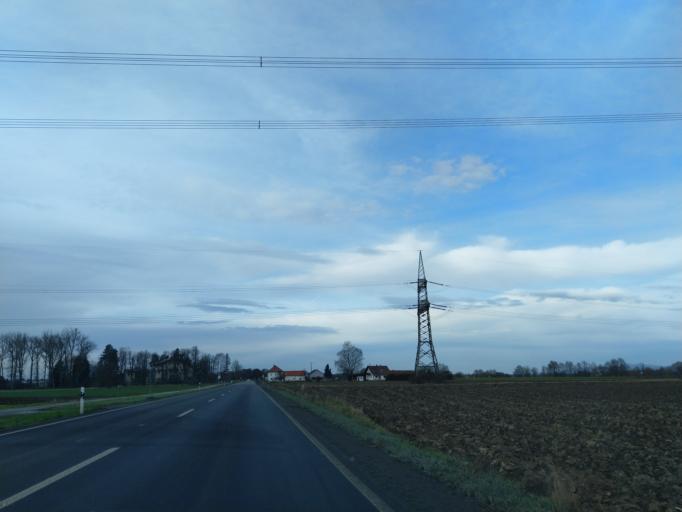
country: DE
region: Bavaria
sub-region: Lower Bavaria
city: Kunzing
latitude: 48.6657
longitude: 13.1004
